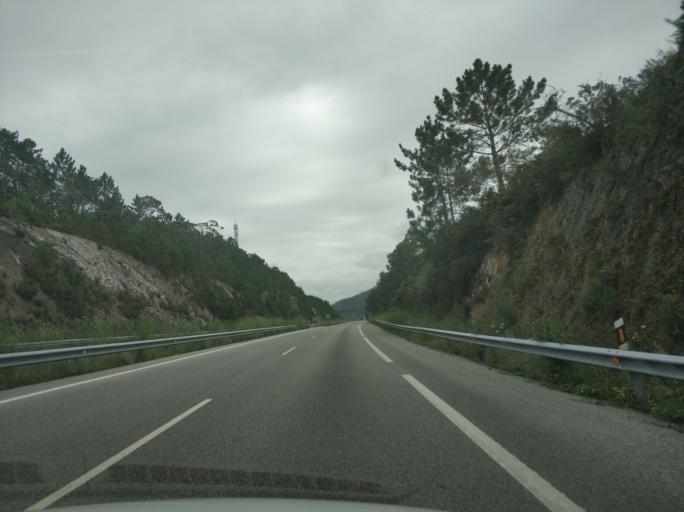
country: ES
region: Asturias
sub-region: Province of Asturias
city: Cudillero
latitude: 43.5659
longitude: -6.2162
